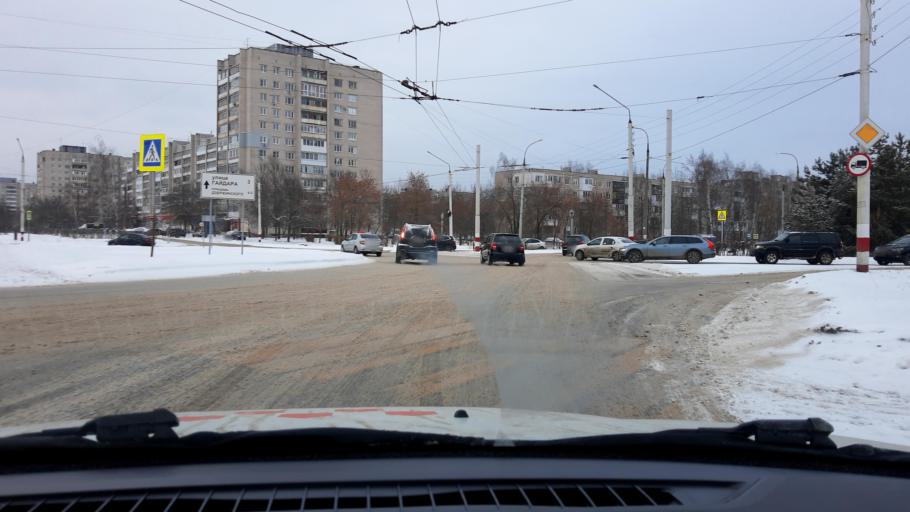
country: RU
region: Nizjnij Novgorod
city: Dzerzhinsk
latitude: 56.2268
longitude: 43.3889
